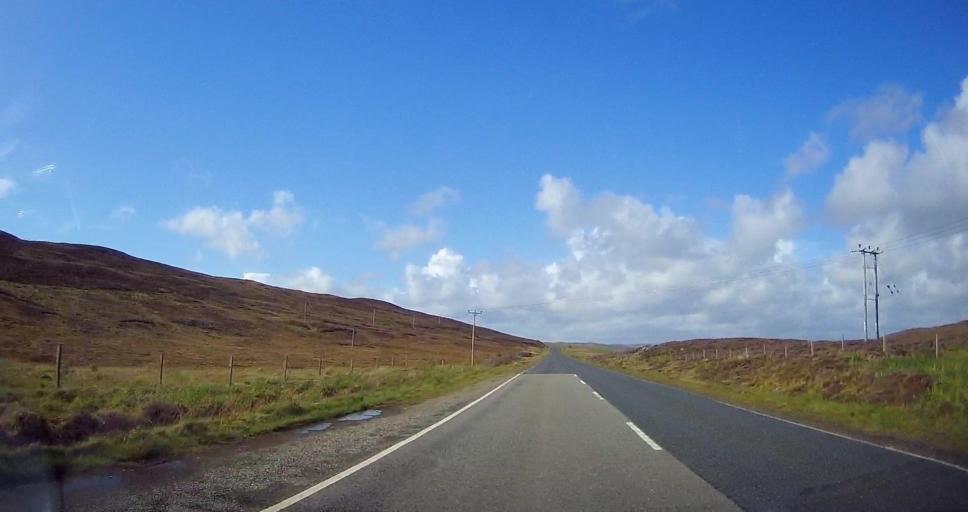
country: GB
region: Scotland
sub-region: Shetland Islands
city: Lerwick
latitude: 60.2098
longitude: -1.2335
